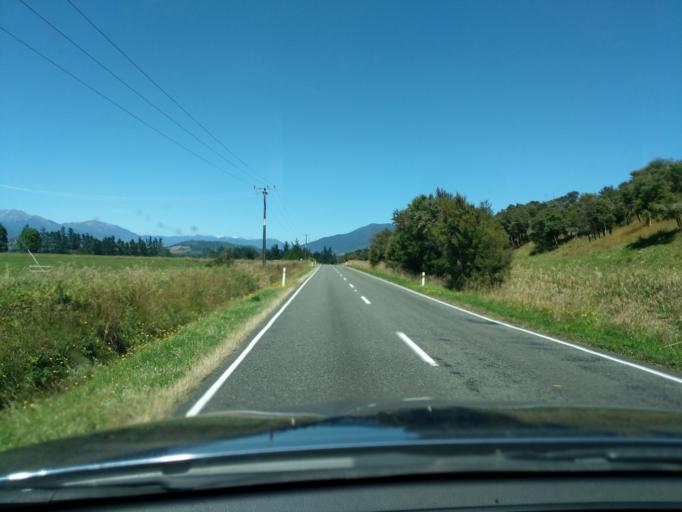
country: NZ
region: Tasman
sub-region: Tasman District
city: Takaka
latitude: -40.6914
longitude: 172.6439
